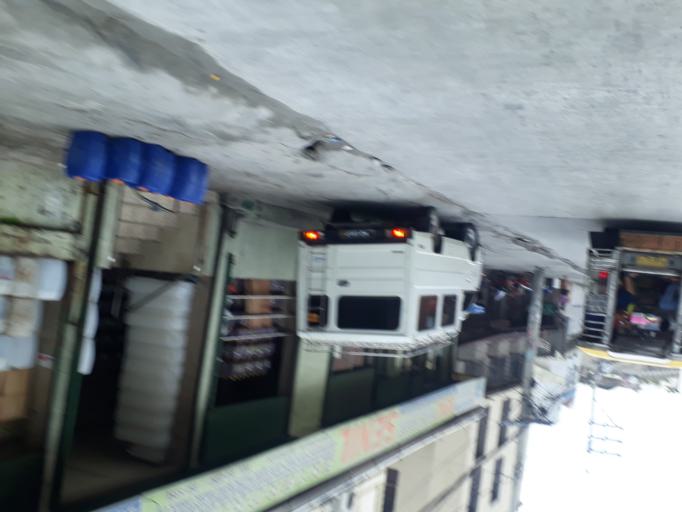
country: PH
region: Metro Manila
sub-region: Caloocan City
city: Niugan
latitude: 14.6603
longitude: 120.9575
